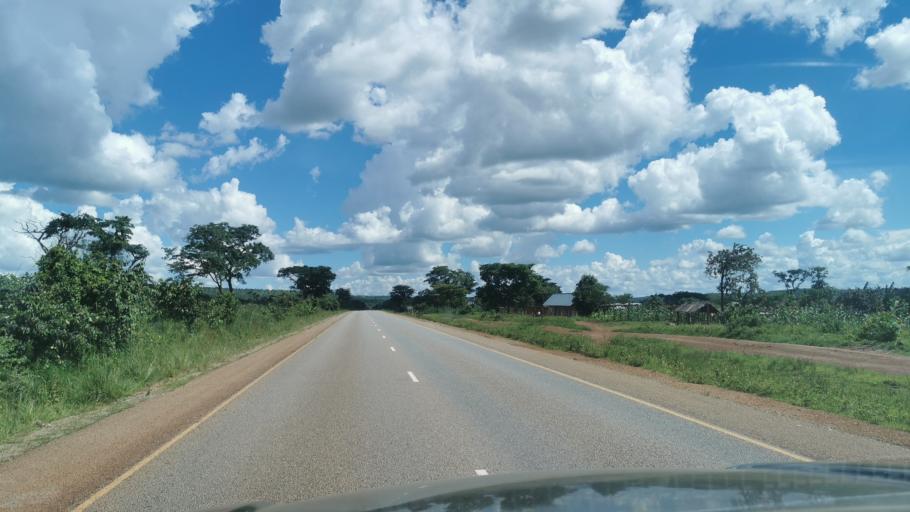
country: TZ
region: Geita
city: Uyovu
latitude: -3.0913
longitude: 31.2958
